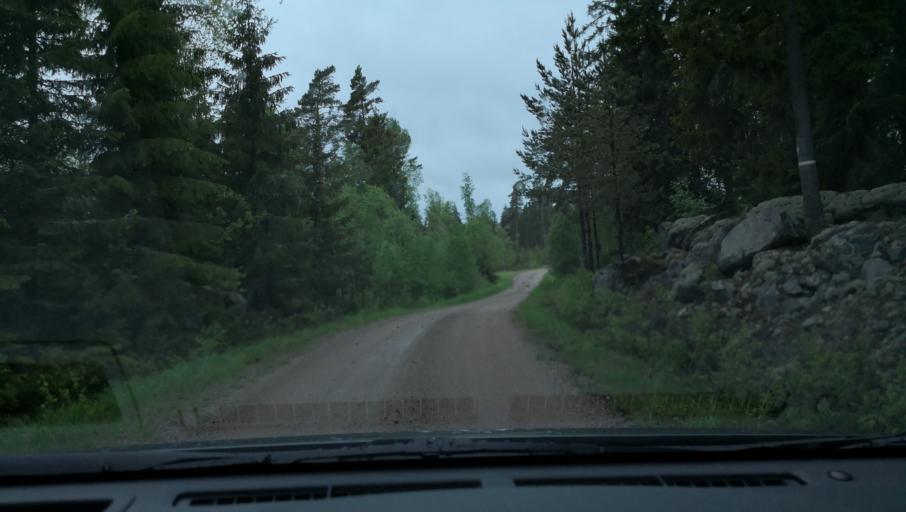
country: SE
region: Uppsala
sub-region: Enkopings Kommun
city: Orsundsbro
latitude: 59.9359
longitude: 17.3147
